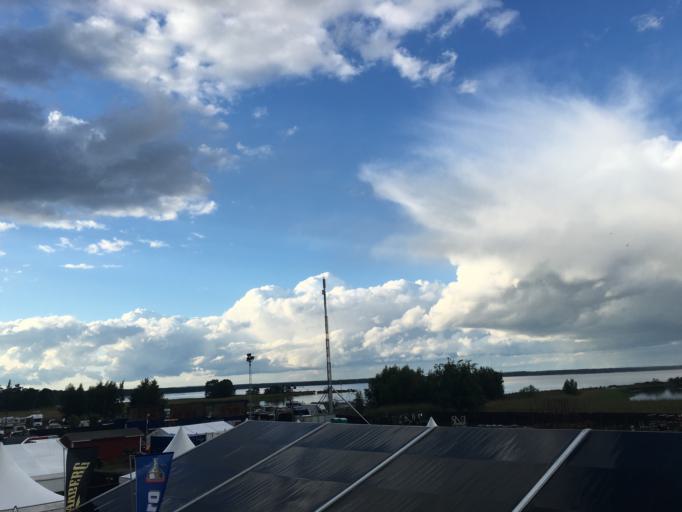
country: SE
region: Blekinge
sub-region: Karlshamns Kommun
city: Morrum
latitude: 56.1211
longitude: 14.6794
